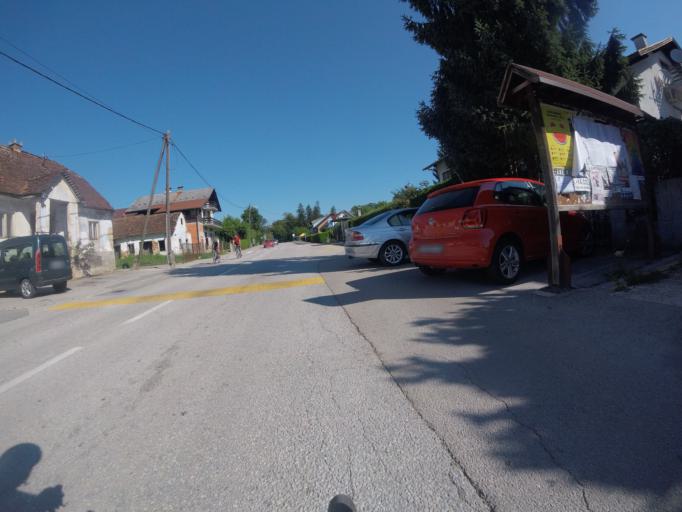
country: HR
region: Zagrebacka
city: Bregana
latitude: 45.8275
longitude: 15.6947
